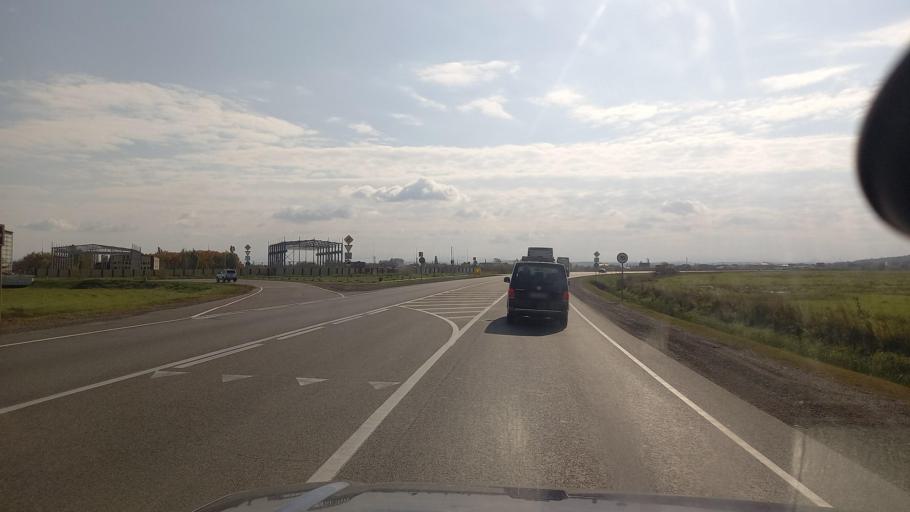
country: RU
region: Krasnodarskiy
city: Abinsk
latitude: 44.8704
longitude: 38.1283
